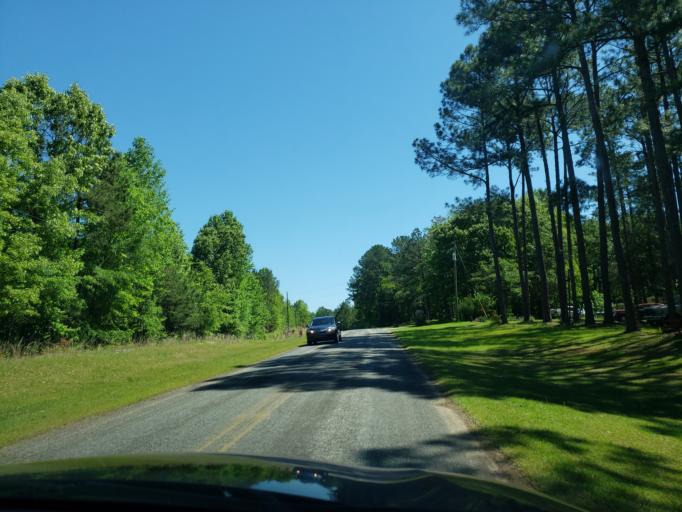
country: US
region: Alabama
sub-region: Elmore County
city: Eclectic
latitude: 32.7036
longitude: -85.8852
